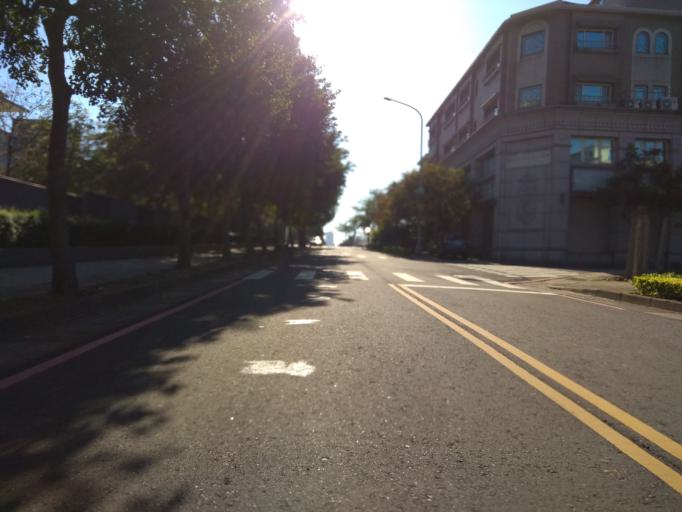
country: TW
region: Taiwan
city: Taoyuan City
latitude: 25.0221
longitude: 121.2202
